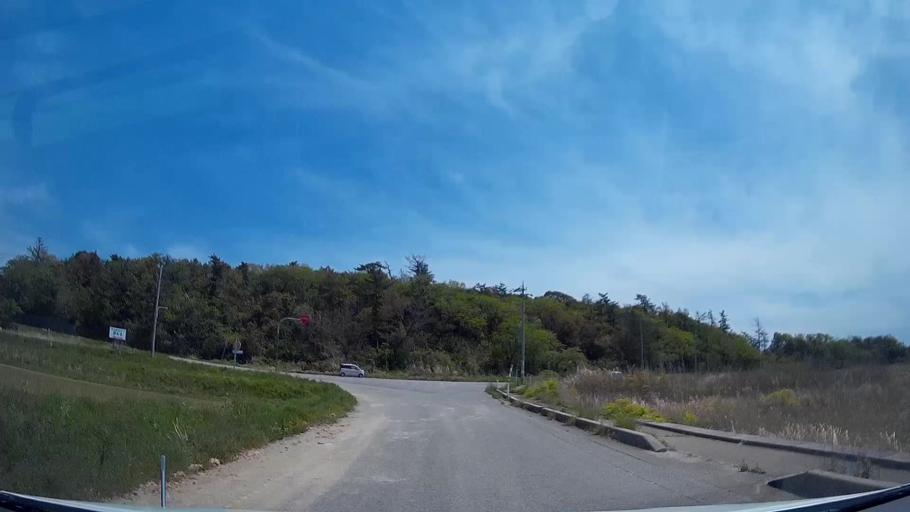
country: JP
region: Ishikawa
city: Hakui
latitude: 36.9412
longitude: 136.7639
